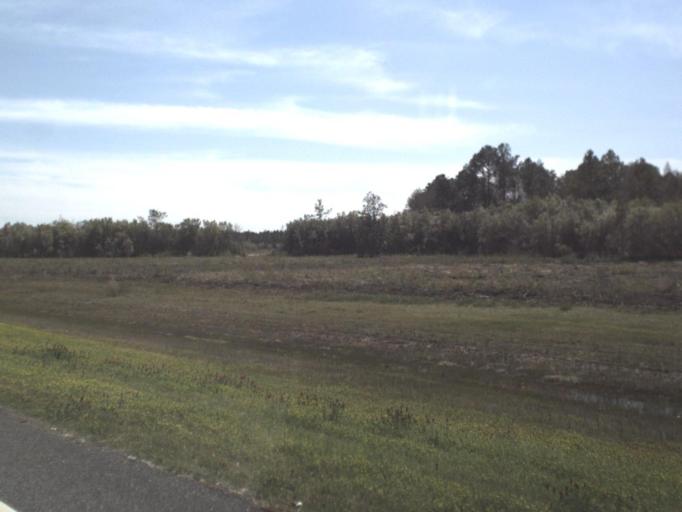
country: US
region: Florida
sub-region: Bay County
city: Lynn Haven
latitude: 30.3588
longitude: -85.6690
